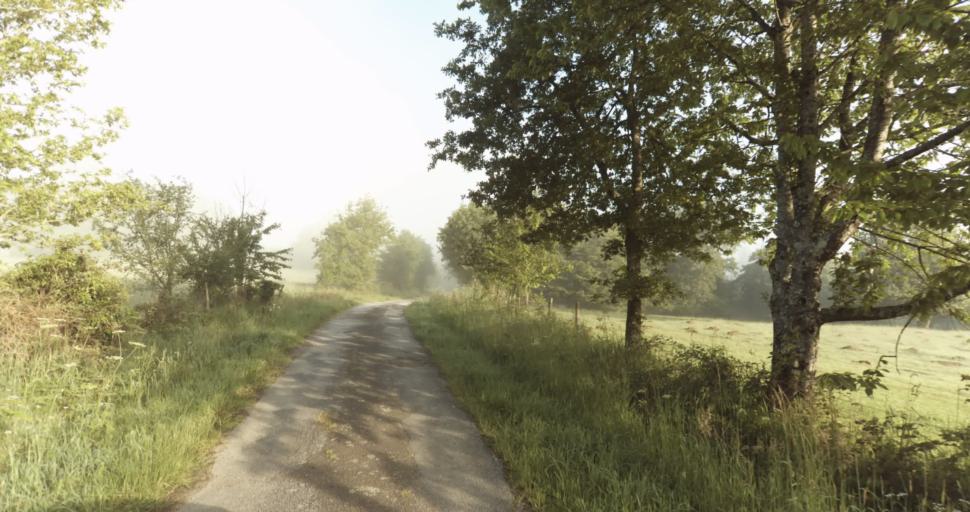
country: FR
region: Limousin
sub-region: Departement de la Haute-Vienne
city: Condat-sur-Vienne
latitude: 45.7856
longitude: 1.2818
